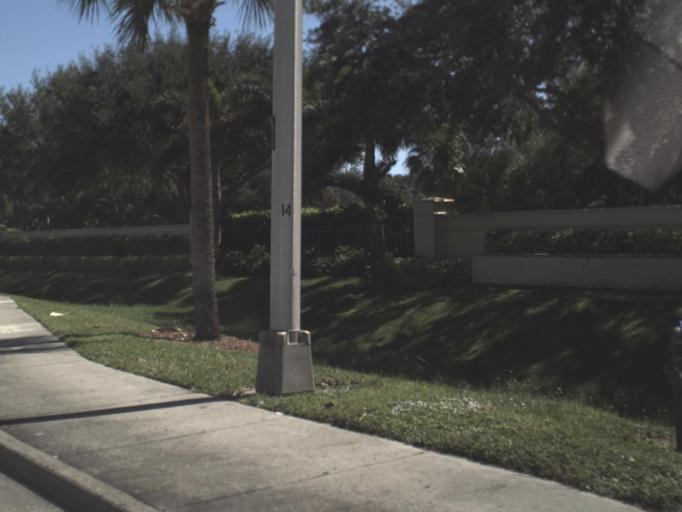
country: US
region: Florida
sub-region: Collier County
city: Pine Ridge
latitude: 26.2116
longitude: -81.7617
